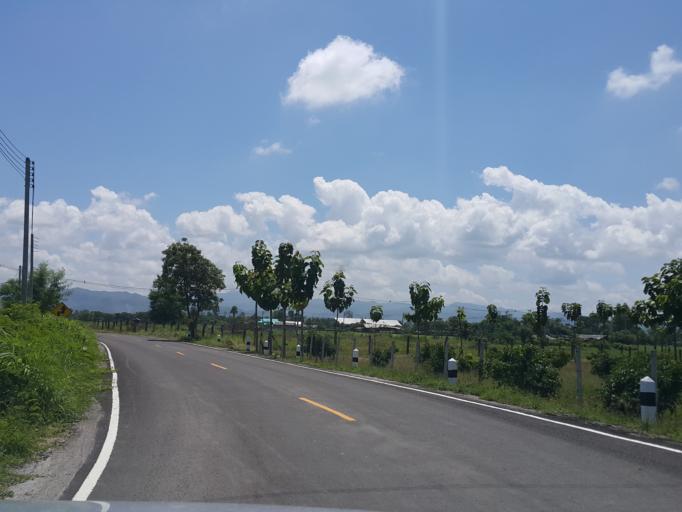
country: TH
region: Lamphun
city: Ban Thi
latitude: 18.6774
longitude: 99.1285
